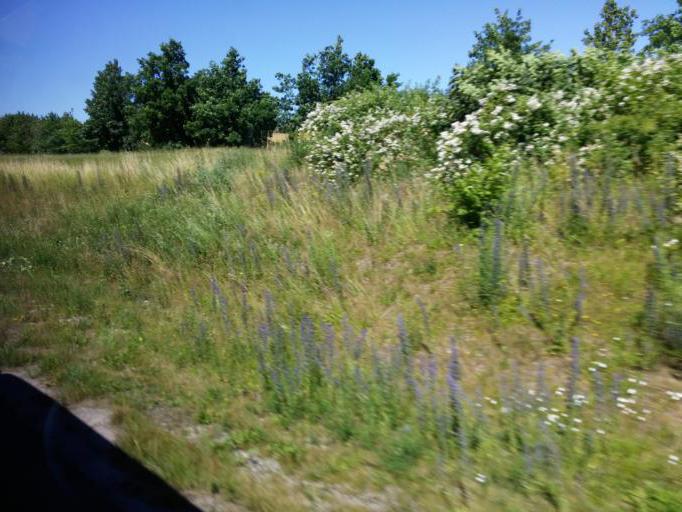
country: SE
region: Skane
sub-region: Malmo
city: Oxie
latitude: 55.5638
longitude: 13.0656
